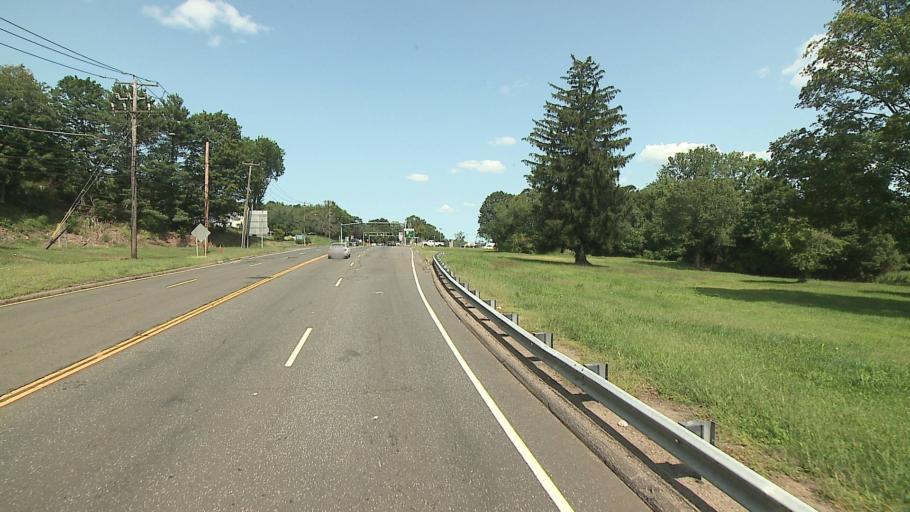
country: US
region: Connecticut
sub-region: New Haven County
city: City of Milford (balance)
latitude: 41.2458
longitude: -73.1024
